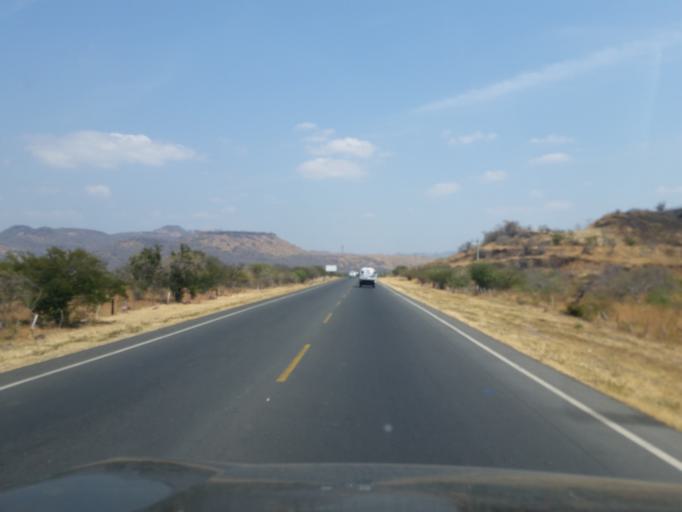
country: NI
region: Managua
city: Tipitapa
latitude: 12.4233
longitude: -86.0415
